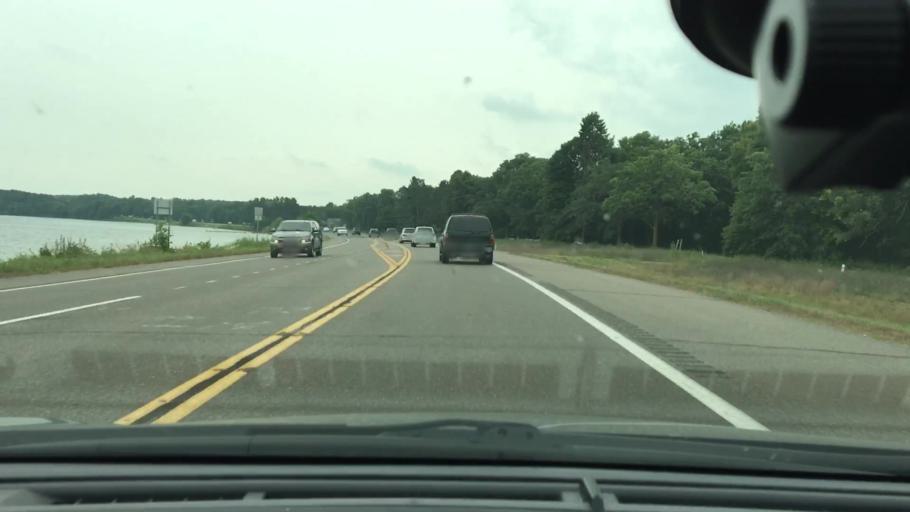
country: US
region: Minnesota
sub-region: Mille Lacs County
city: Vineland
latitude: 46.2139
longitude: -93.7927
